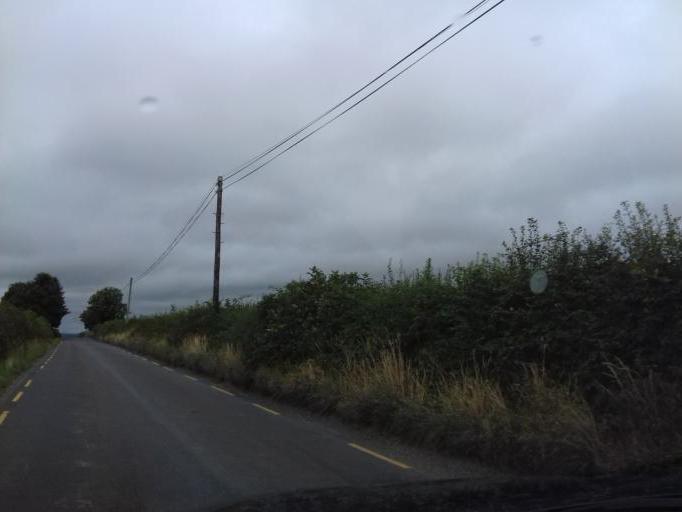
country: IE
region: Leinster
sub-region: County Carlow
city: Bagenalstown
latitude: 52.6193
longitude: -7.0375
